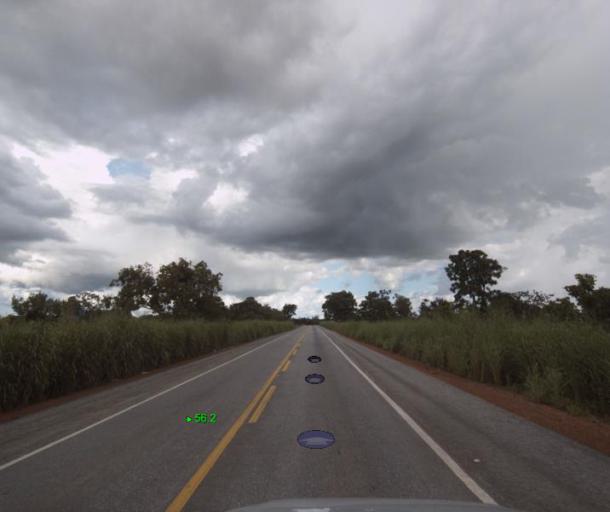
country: BR
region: Goias
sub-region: Porangatu
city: Porangatu
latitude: -13.3072
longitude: -49.1191
